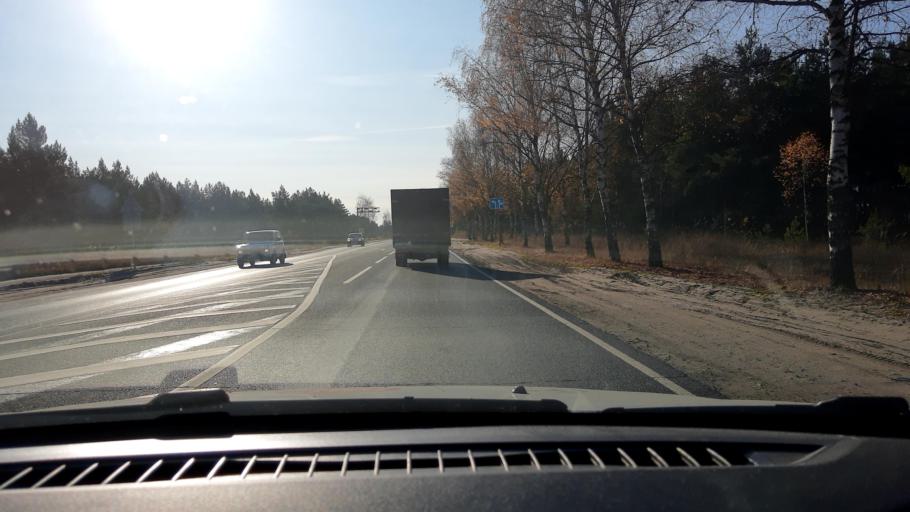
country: RU
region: Nizjnij Novgorod
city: Dzerzhinsk
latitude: 56.2900
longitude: 43.4758
